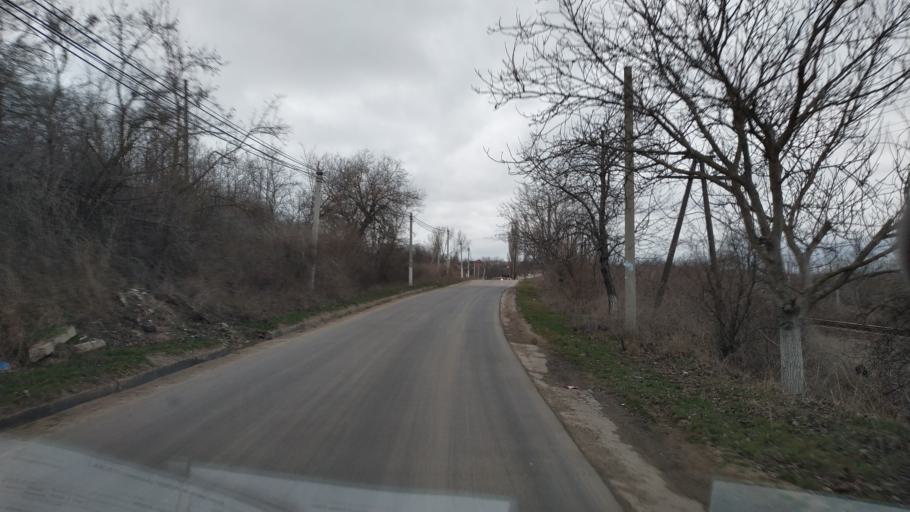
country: MD
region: Bender
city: Bender
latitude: 46.7671
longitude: 29.4811
